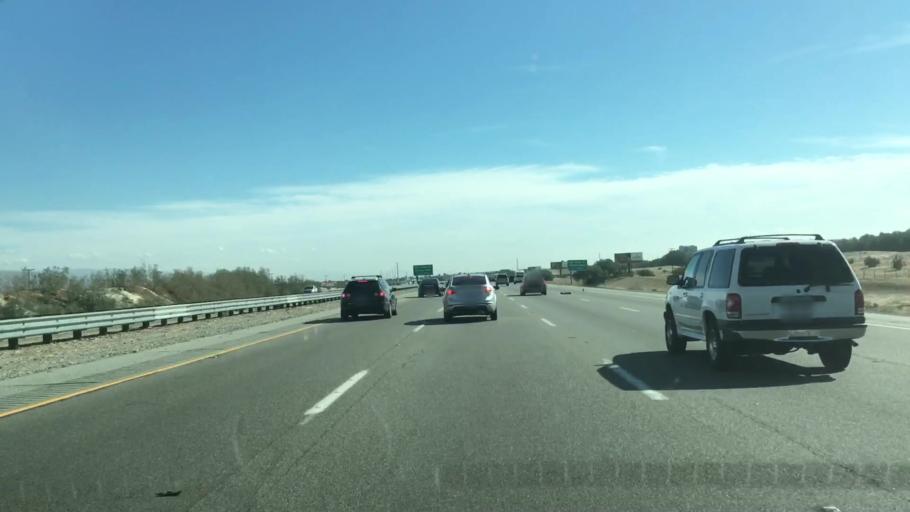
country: US
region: California
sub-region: Riverside County
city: Thousand Palms
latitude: 33.8295
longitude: -116.4250
